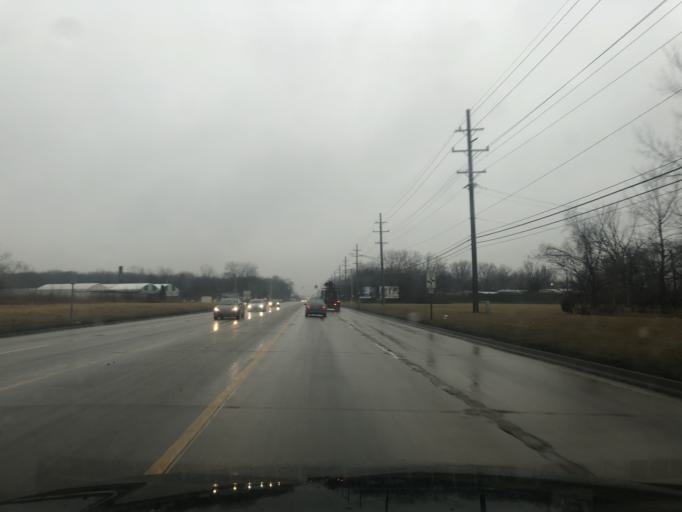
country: US
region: Michigan
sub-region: Wayne County
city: Inkster
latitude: 42.2676
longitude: -83.3387
